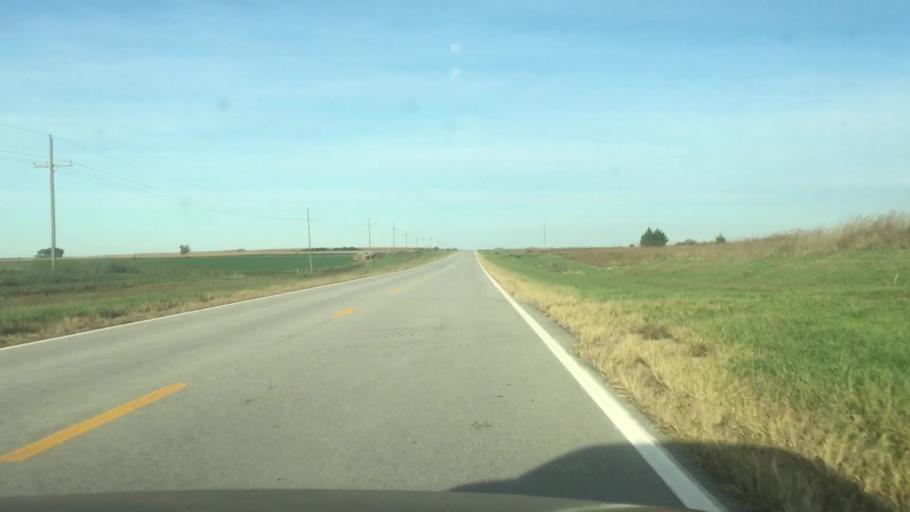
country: US
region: Nebraska
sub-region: Gage County
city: Wymore
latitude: 40.0450
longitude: -96.7202
